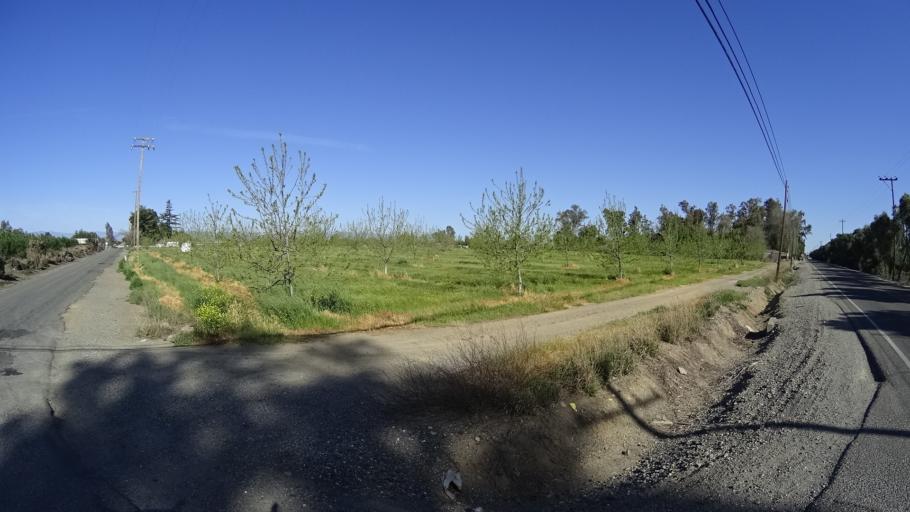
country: US
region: California
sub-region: Glenn County
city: Orland
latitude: 39.7113
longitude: -122.1972
